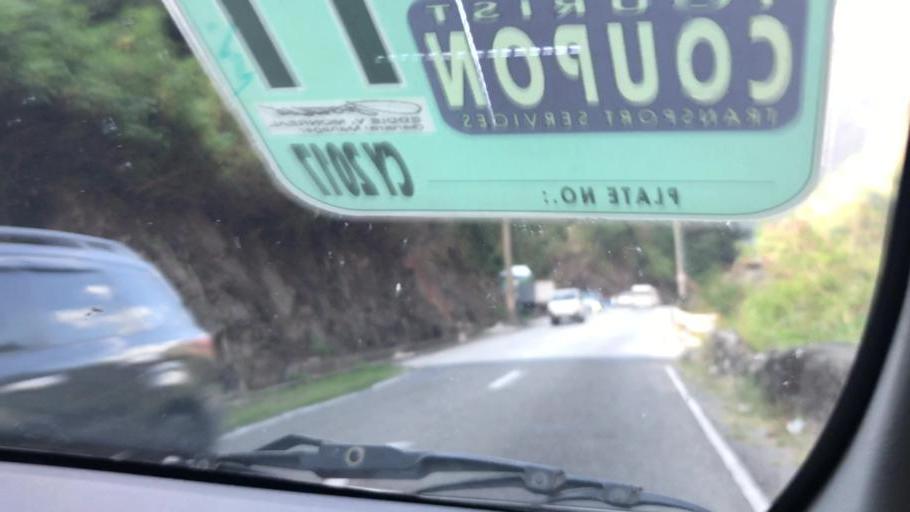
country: PH
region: Cordillera
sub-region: Province of Benguet
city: Tuba
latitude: 16.3233
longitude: 120.6150
